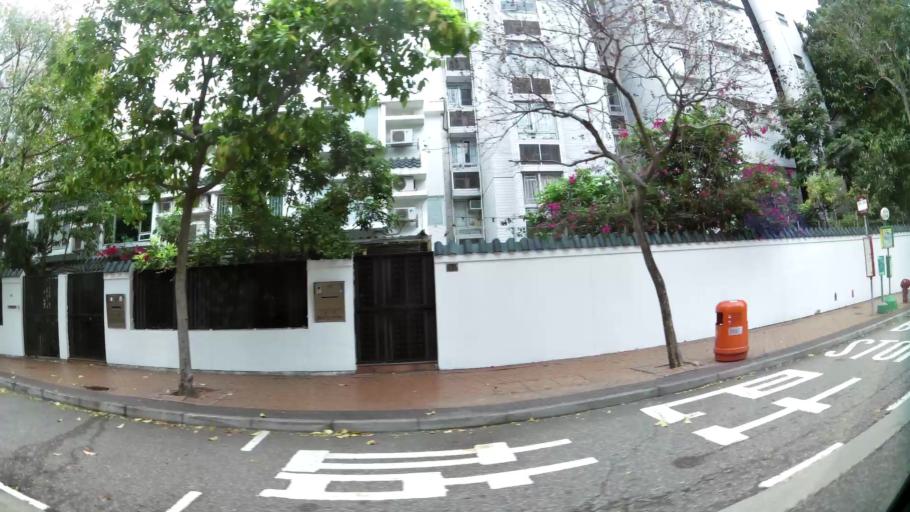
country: HK
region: Sham Shui Po
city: Sham Shui Po
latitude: 22.3331
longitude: 114.1755
